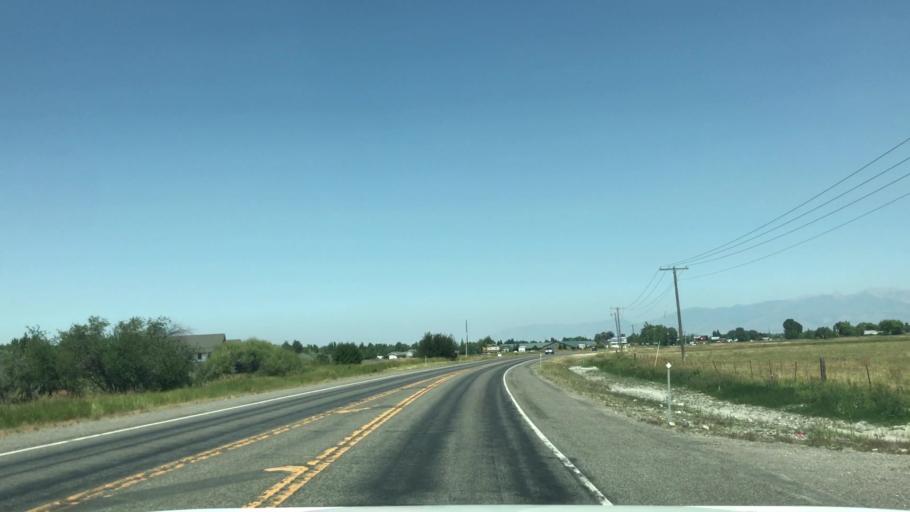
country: US
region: Montana
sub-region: Gallatin County
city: Four Corners
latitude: 45.6408
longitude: -111.1965
